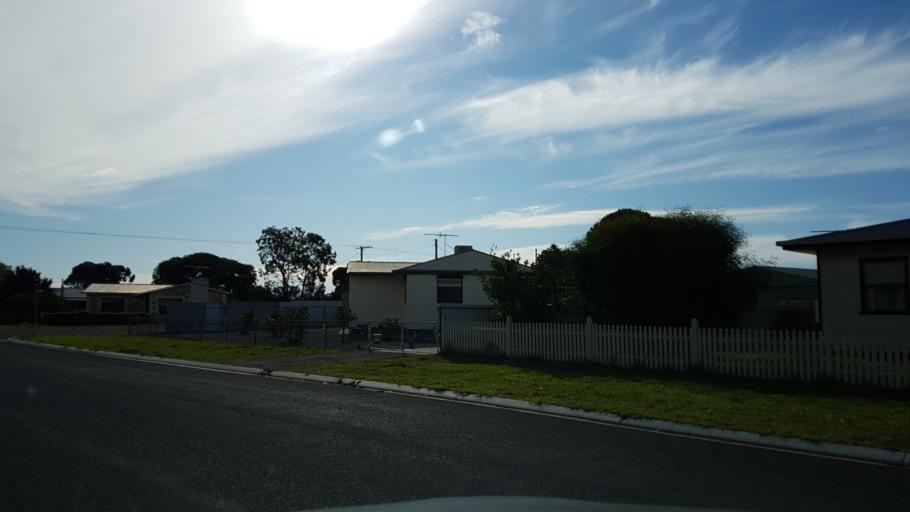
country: AU
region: South Australia
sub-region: Murray Bridge
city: Tailem Bend
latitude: -35.2526
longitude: 139.4627
